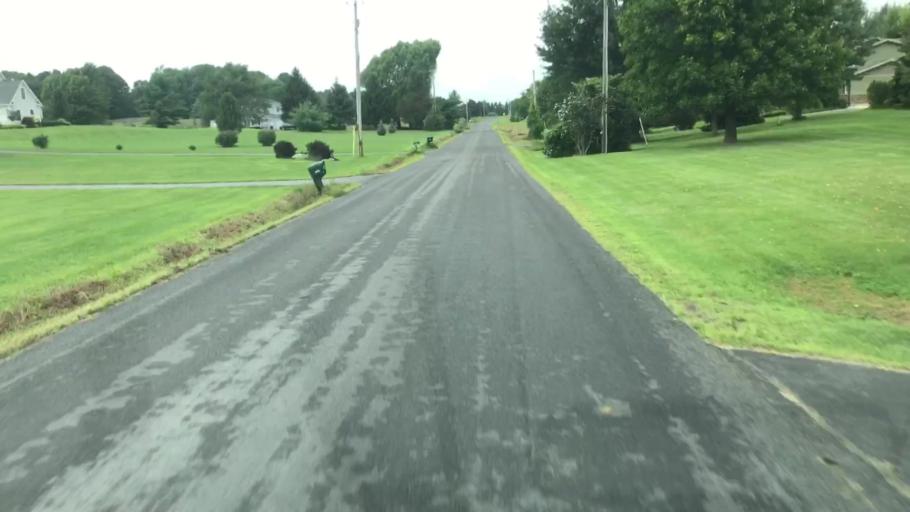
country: US
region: New York
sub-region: Cayuga County
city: Auburn
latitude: 42.9740
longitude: -76.5090
